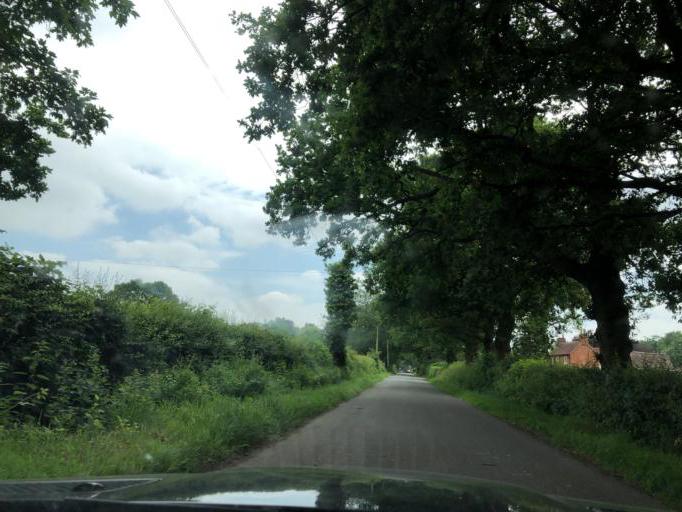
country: GB
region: England
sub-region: Warwickshire
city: Wroxall
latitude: 52.3377
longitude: -1.6477
